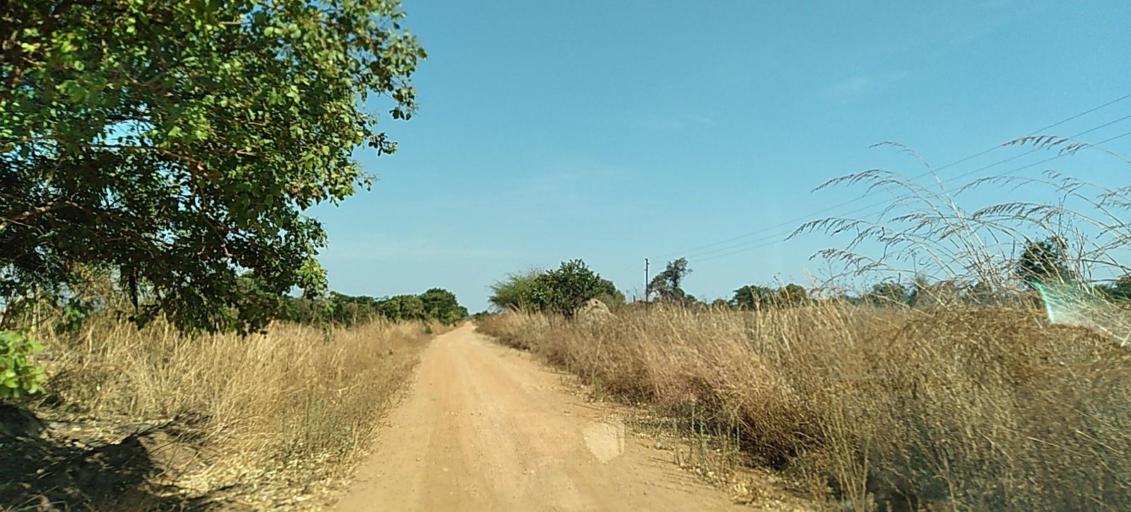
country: ZM
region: Copperbelt
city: Chililabombwe
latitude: -12.3494
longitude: 27.8806
